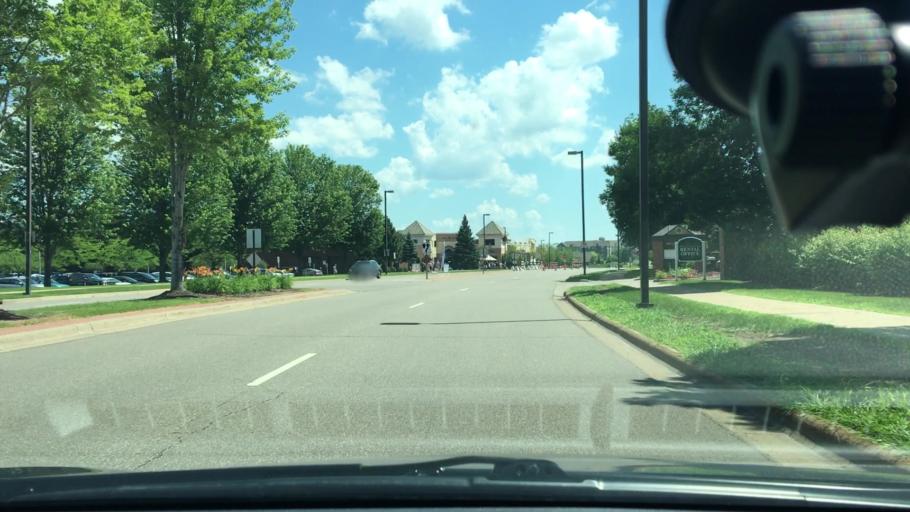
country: US
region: Minnesota
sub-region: Hennepin County
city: Maple Grove
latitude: 45.0982
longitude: -93.4440
